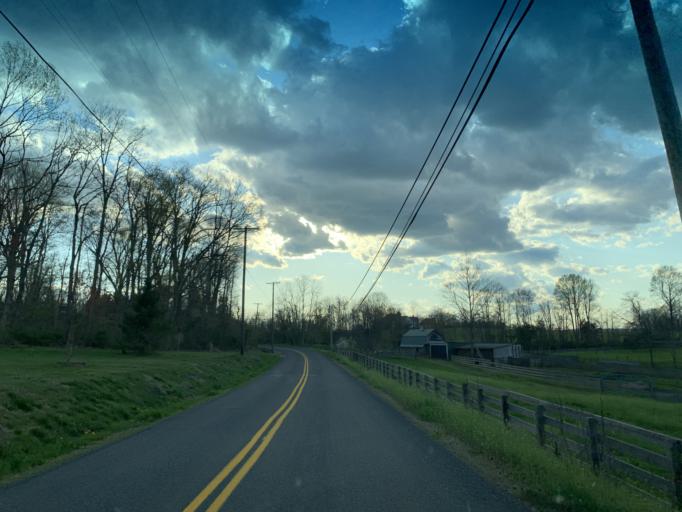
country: US
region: Maryland
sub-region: Harford County
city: South Bel Air
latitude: 39.6054
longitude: -76.3078
